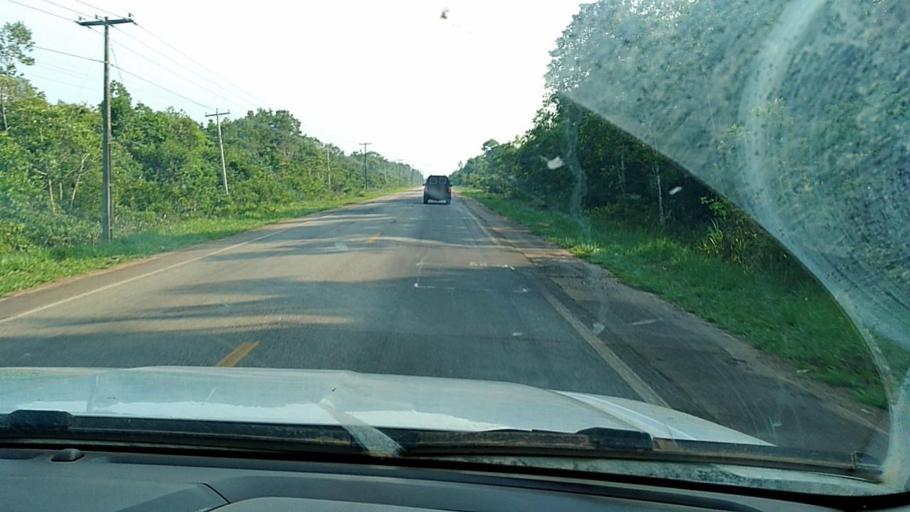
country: BR
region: Rondonia
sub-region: Porto Velho
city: Porto Velho
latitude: -8.3250
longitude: -63.9489
